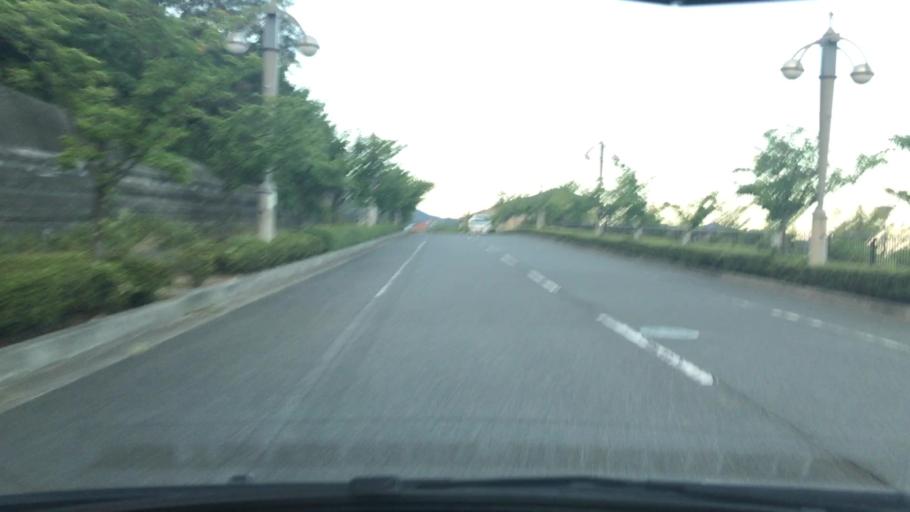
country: JP
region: Hyogo
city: Takarazuka
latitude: 34.8345
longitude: 135.3057
